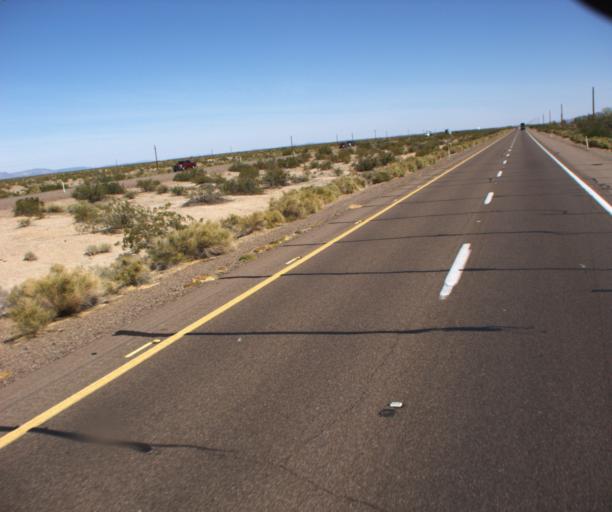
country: US
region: Arizona
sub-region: Yuma County
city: Wellton
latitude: 32.7393
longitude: -113.6910
